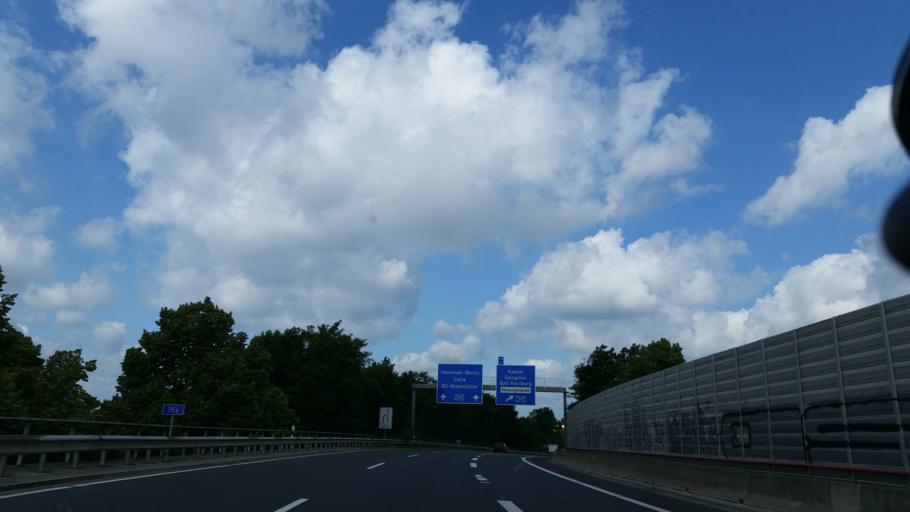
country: DE
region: Lower Saxony
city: Braunschweig
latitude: 52.2816
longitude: 10.5053
